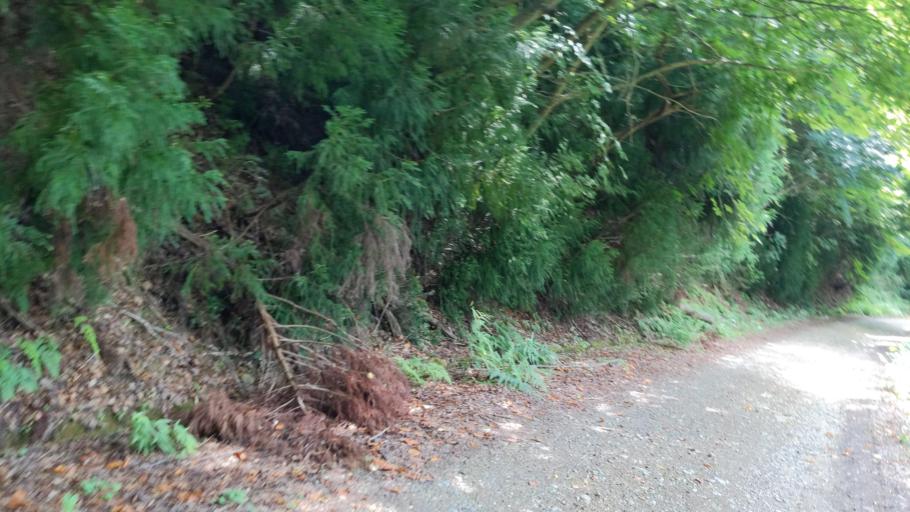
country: JP
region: Kyoto
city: Maizuru
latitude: 35.3916
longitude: 135.4403
